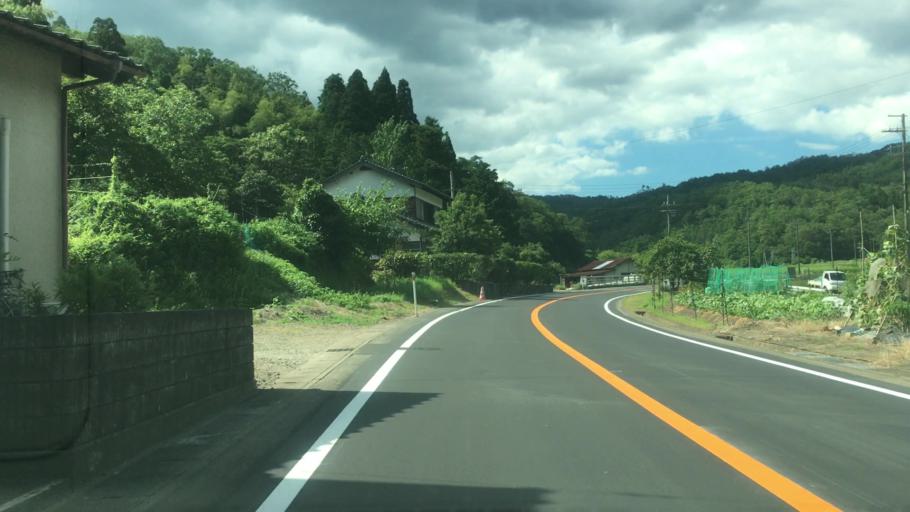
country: JP
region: Hyogo
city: Toyooka
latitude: 35.5011
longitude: 134.7774
